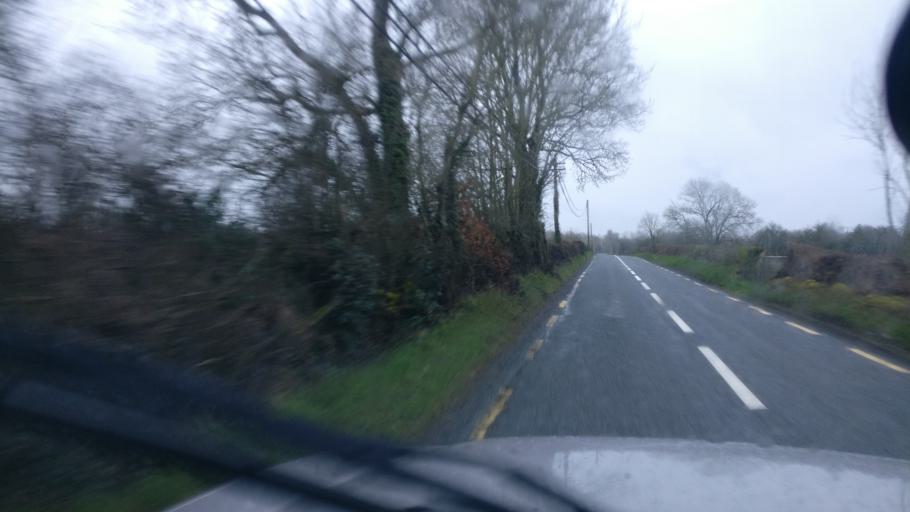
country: IE
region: Connaught
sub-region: County Galway
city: Ballinasloe
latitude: 53.2284
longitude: -8.1914
